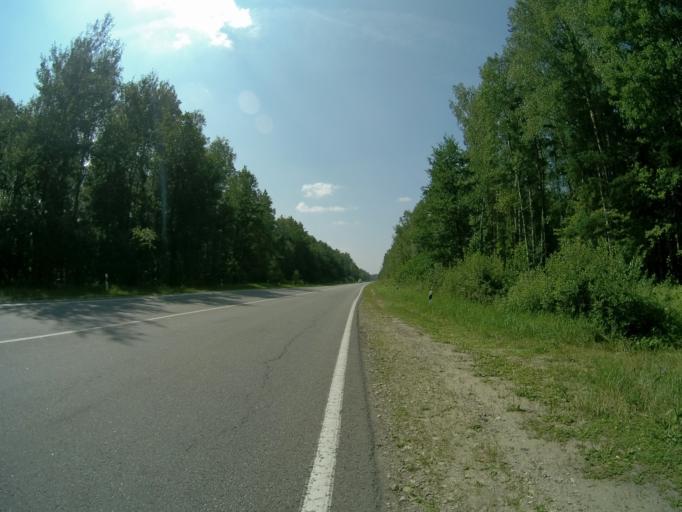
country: RU
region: Vladimir
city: Anopino
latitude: 55.6669
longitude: 40.7344
